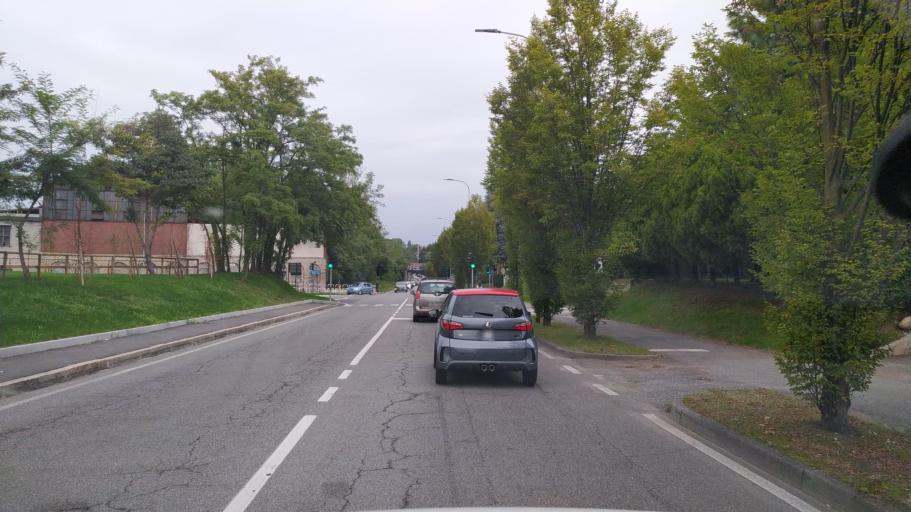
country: IT
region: Lombardy
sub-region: Provincia di Monza e Brianza
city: Seregno
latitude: 45.6402
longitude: 9.2065
